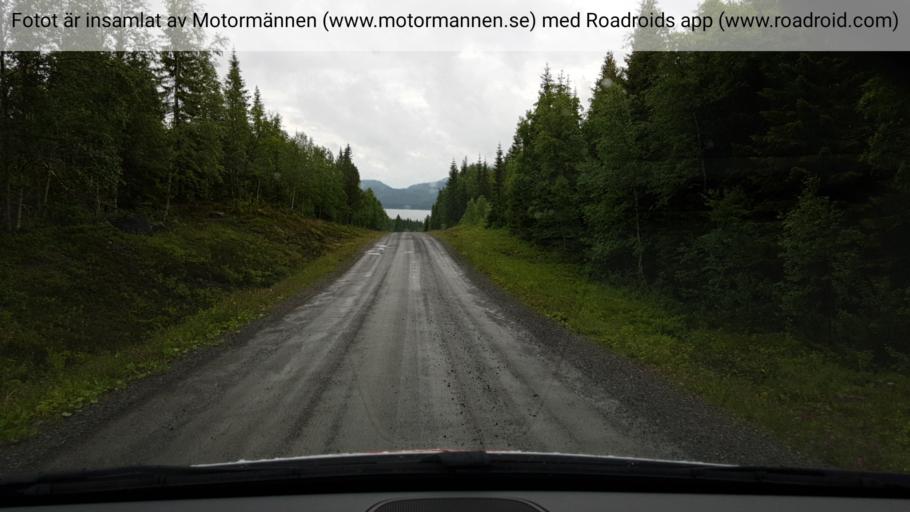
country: SE
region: Jaemtland
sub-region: Stroemsunds Kommun
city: Stroemsund
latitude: 64.2486
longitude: 15.0363
